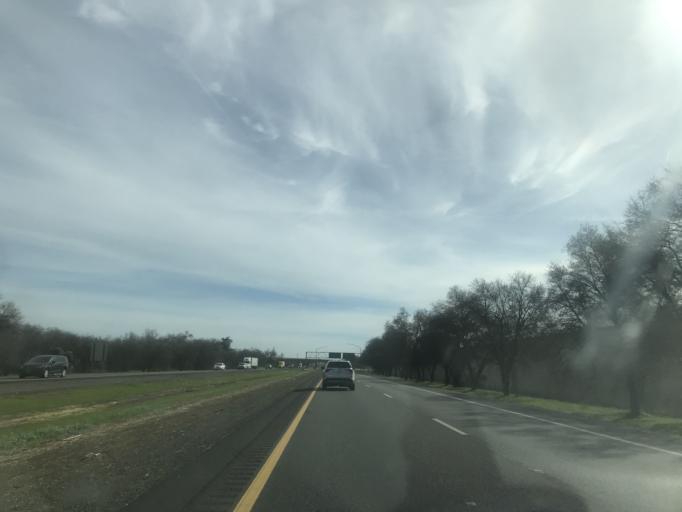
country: US
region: California
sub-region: Yolo County
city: Woodland
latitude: 38.6883
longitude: -121.7540
